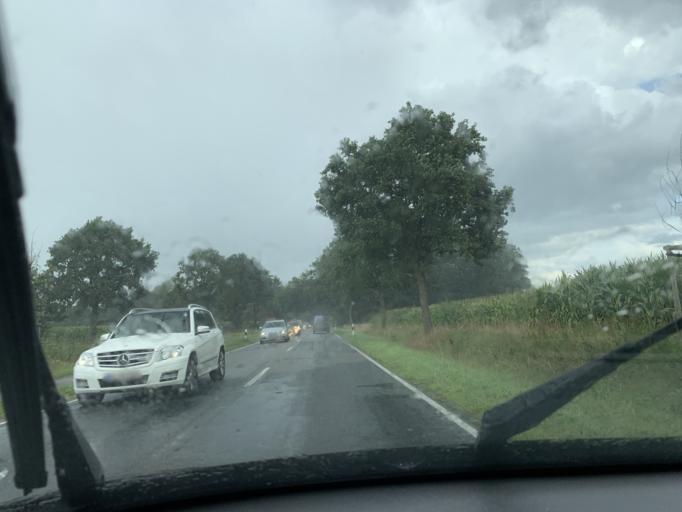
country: DE
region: Lower Saxony
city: Wiefelstede
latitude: 53.3004
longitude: 8.0550
